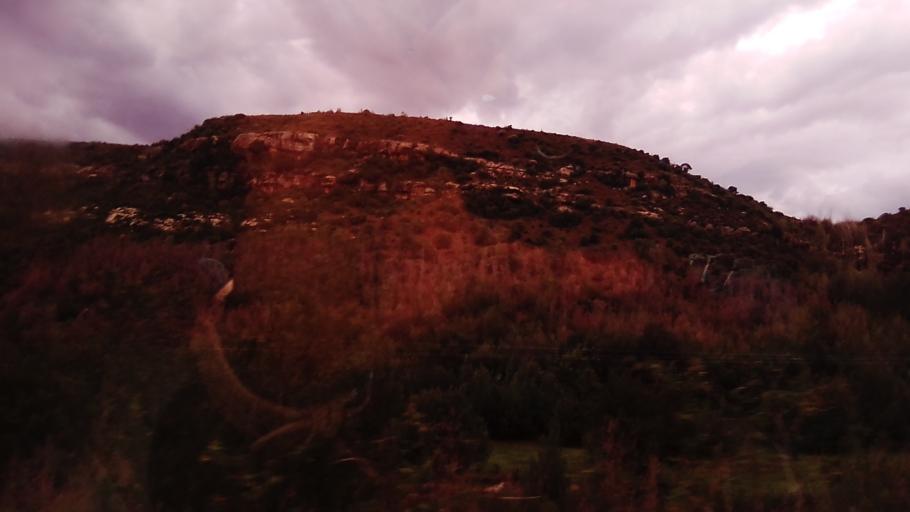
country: LS
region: Berea
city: Teyateyaneng
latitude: -29.3308
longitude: 27.7033
